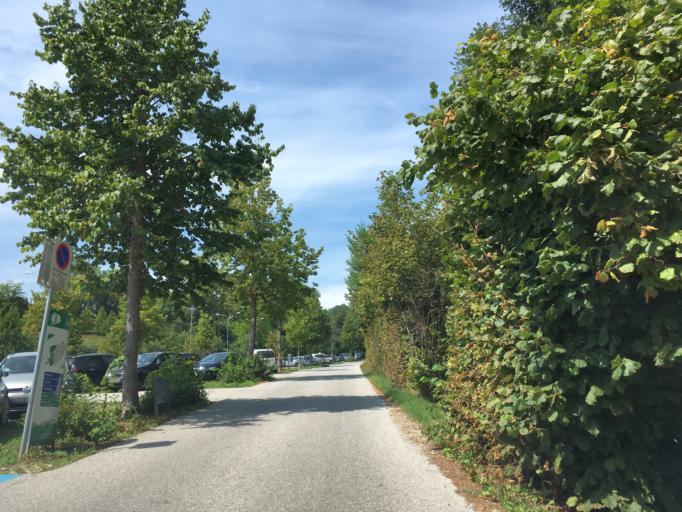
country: AT
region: Styria
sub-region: Politischer Bezirk Hartberg-Fuerstenfeld
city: Hartberg
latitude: 47.2787
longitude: 15.9659
